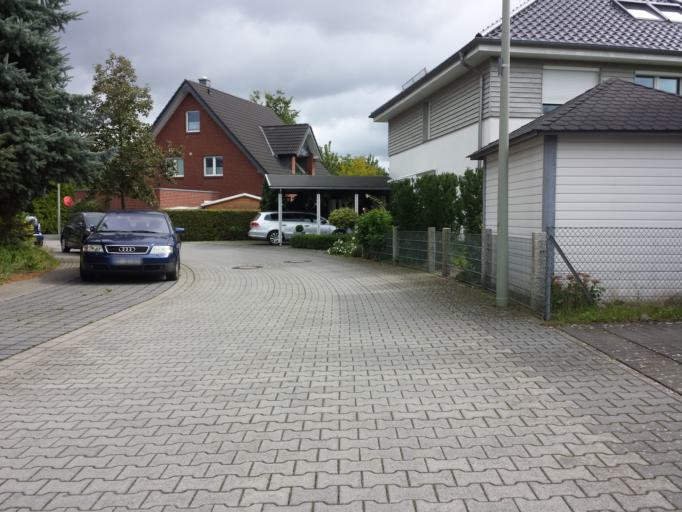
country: DE
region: North Rhine-Westphalia
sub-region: Regierungsbezirk Detmold
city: Guetersloh
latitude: 51.8827
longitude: 8.4022
